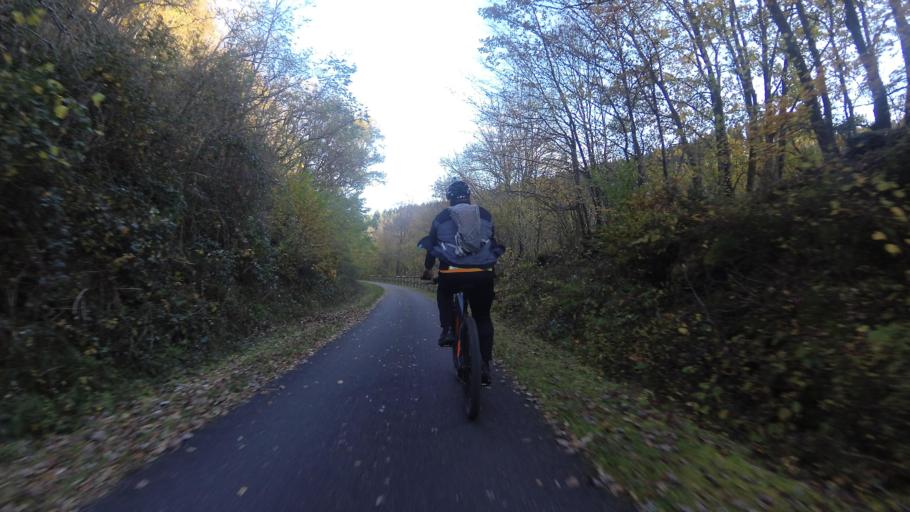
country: DE
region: Rheinland-Pfalz
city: Ollmuth
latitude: 49.6548
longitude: 6.7219
